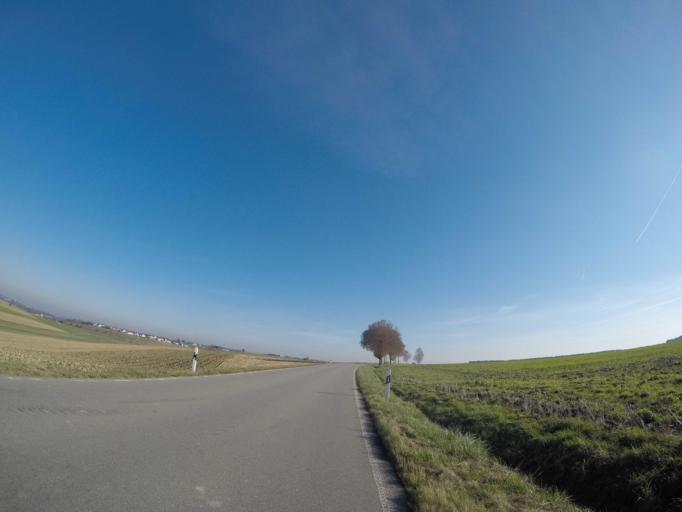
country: DE
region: Baden-Wuerttemberg
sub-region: Tuebingen Region
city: Unterwachingen
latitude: 48.2075
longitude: 9.6364
